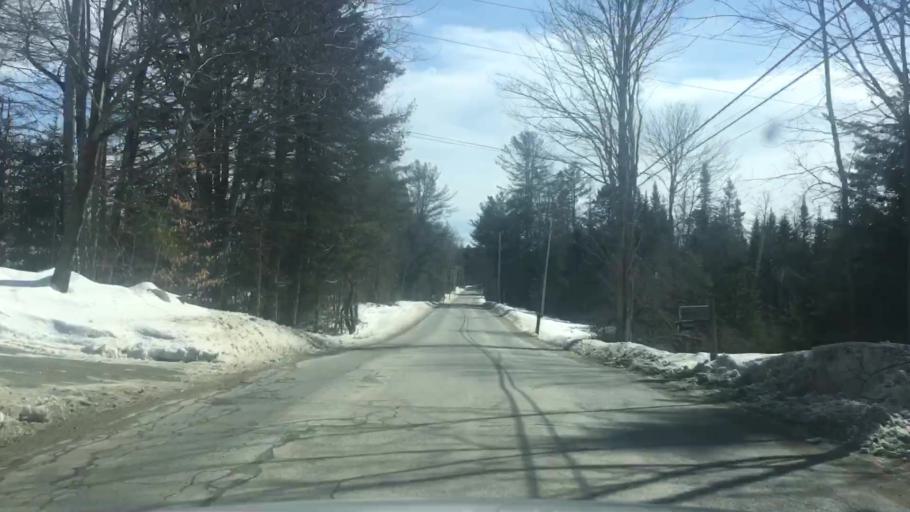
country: US
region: Maine
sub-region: Penobscot County
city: Holden
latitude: 44.7569
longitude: -68.6379
